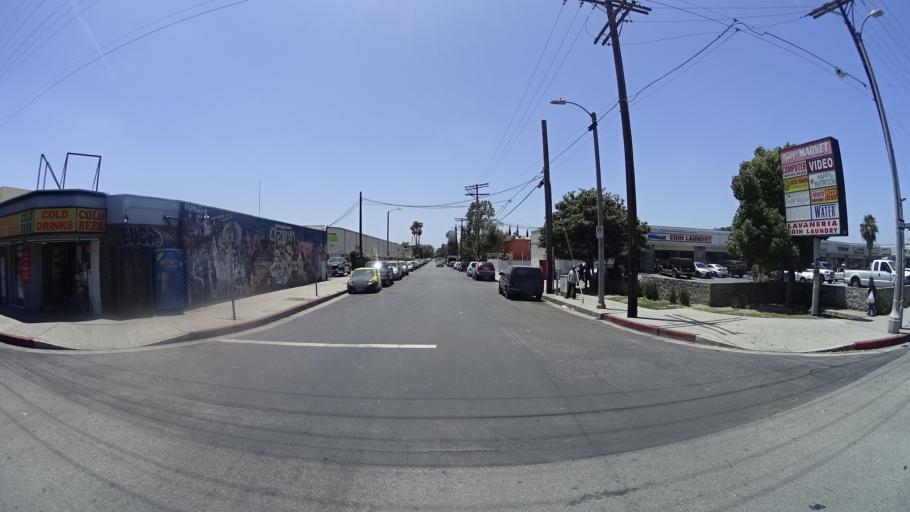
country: US
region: California
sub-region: Los Angeles County
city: Van Nuys
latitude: 34.2281
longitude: -118.4537
